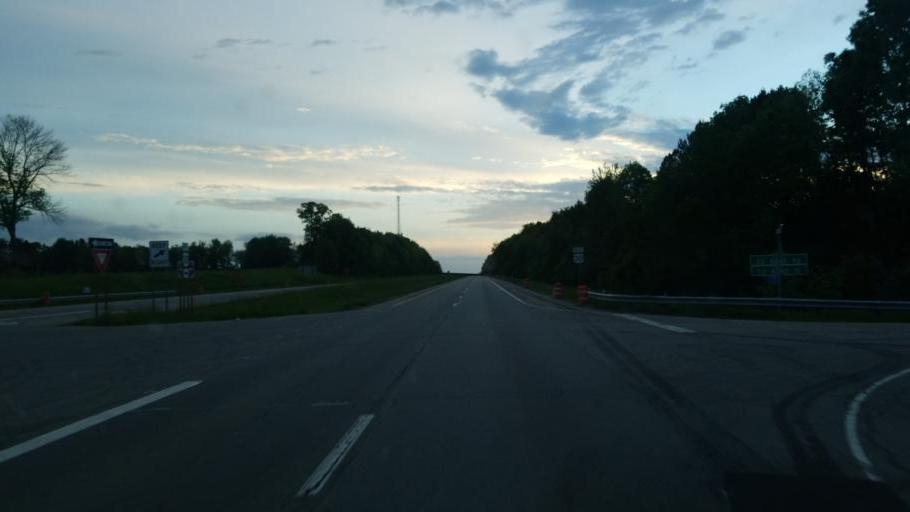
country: US
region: Ohio
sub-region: Wayne County
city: Shreve
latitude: 40.7845
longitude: -82.1268
